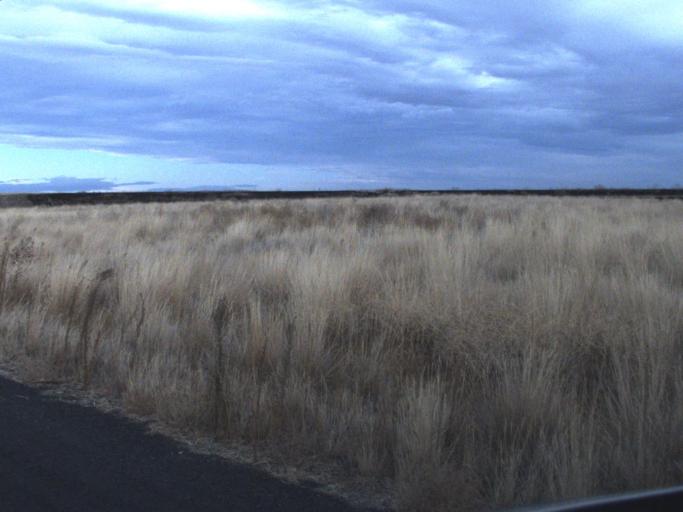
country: US
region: Washington
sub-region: Adams County
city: Ritzville
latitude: 47.4455
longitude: -118.7359
